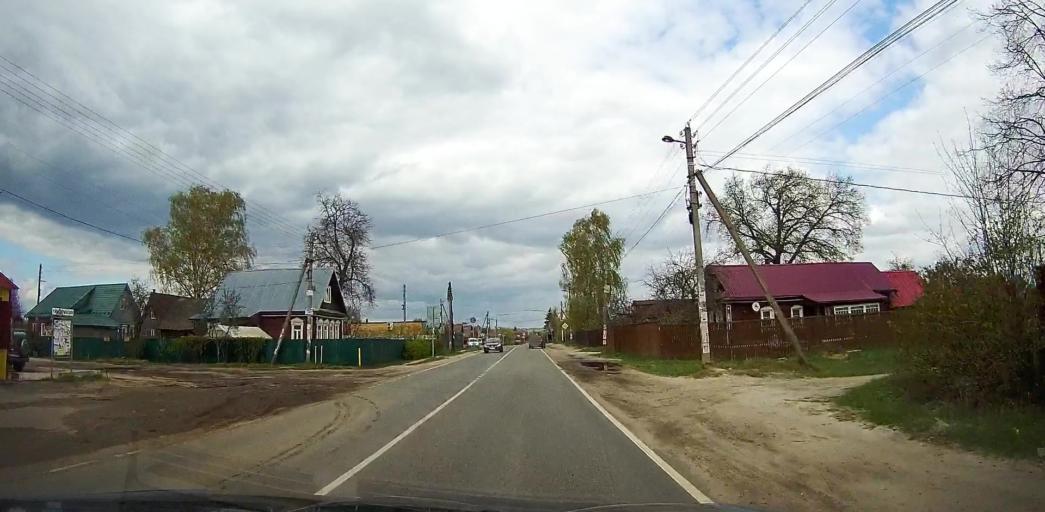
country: RU
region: Moskovskaya
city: Ashitkovo
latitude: 55.4480
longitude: 38.5923
